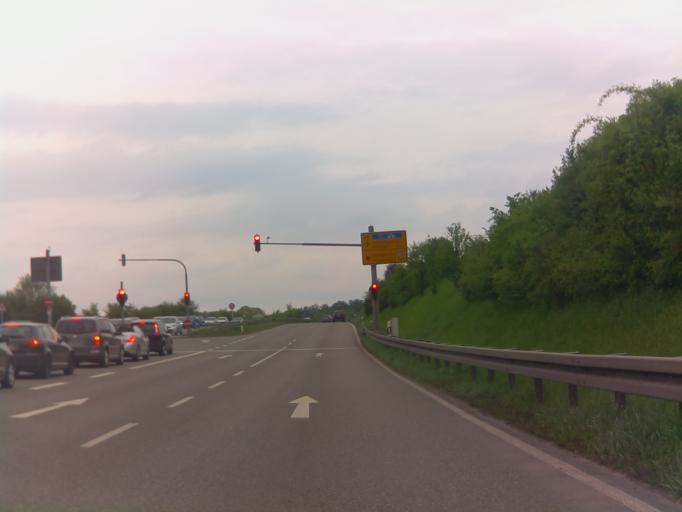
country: DE
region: Baden-Wuerttemberg
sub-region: Regierungsbezirk Stuttgart
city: Holzgerlingen
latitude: 48.6468
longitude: 9.0086
